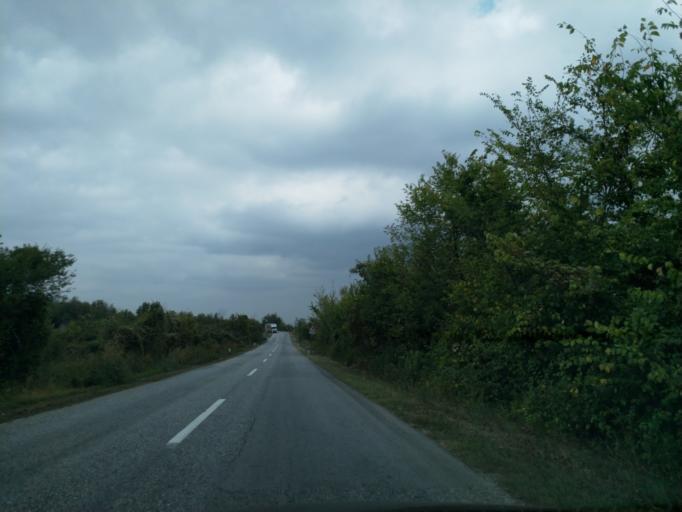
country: RS
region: Central Serbia
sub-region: Sumadijski Okrug
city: Topola
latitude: 44.1503
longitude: 20.7414
